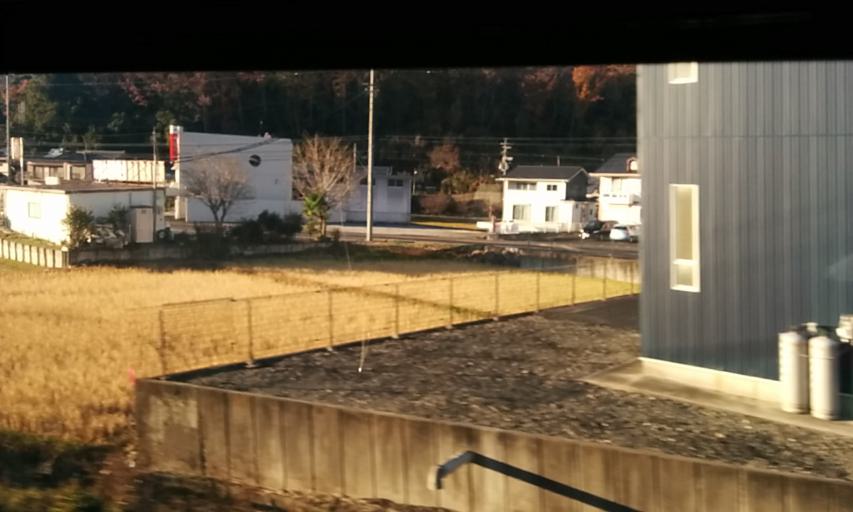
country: JP
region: Gifu
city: Mizunami
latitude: 35.3650
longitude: 137.2331
